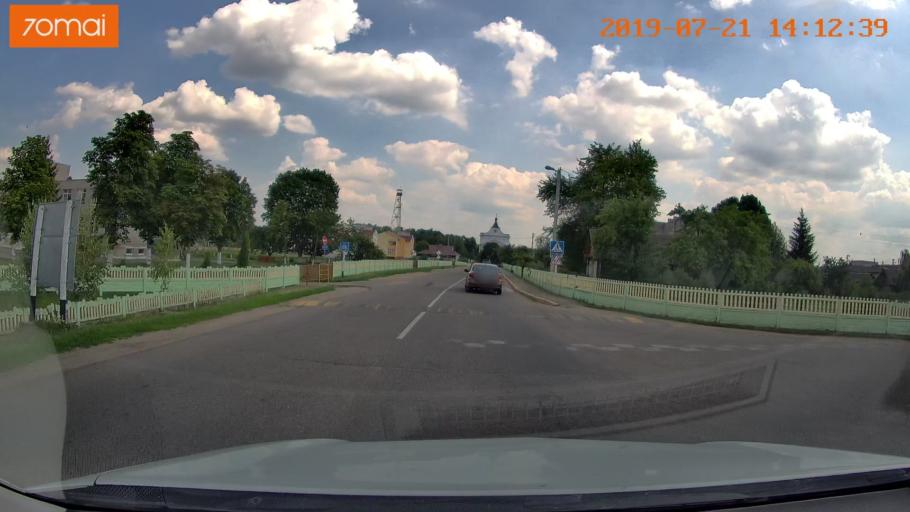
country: BY
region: Grodnenskaya
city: Karelichy
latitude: 53.6518
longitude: 26.1700
